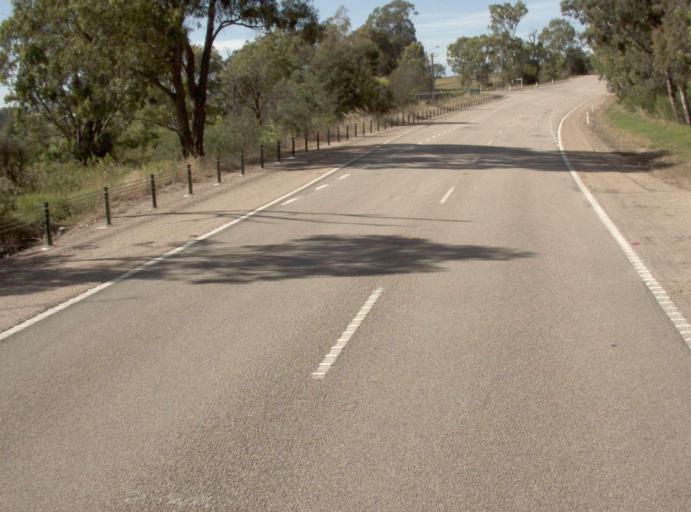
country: AU
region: Victoria
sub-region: East Gippsland
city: Bairnsdale
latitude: -37.7183
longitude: 147.8052
